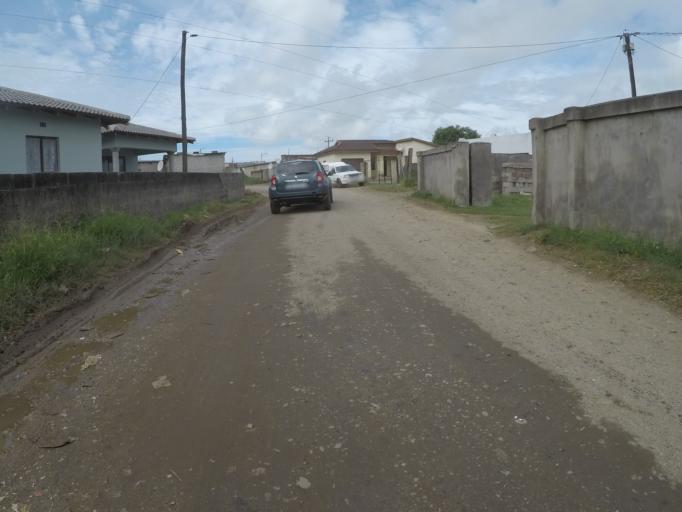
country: ZA
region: KwaZulu-Natal
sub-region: uThungulu District Municipality
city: eSikhawini
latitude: -28.8598
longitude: 31.9174
